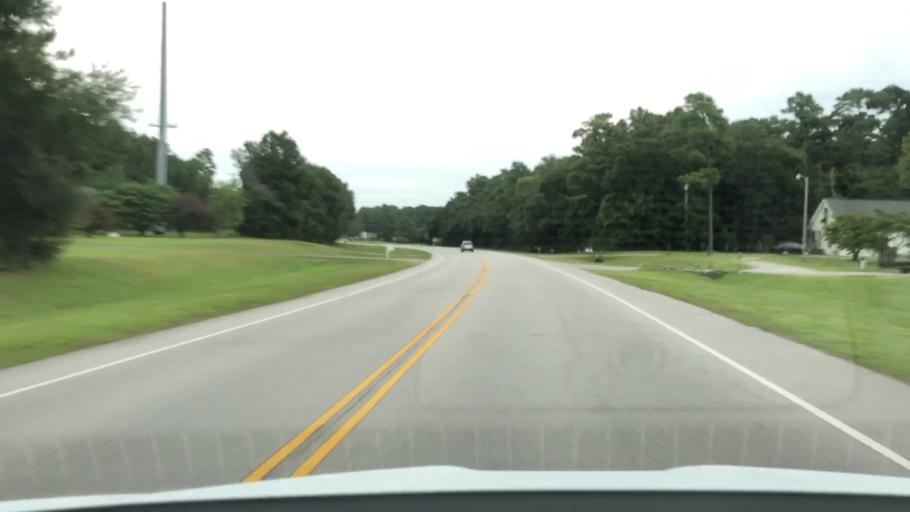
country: US
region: North Carolina
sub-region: Carteret County
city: Cape Carteret
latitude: 34.7017
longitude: -77.0678
